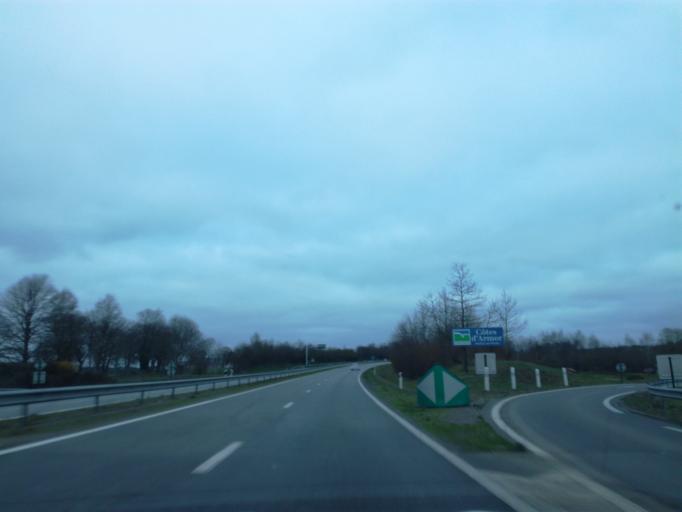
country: FR
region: Brittany
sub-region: Departement du Morbihan
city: Saint-Gonnery
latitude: 48.1366
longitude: -2.7958
